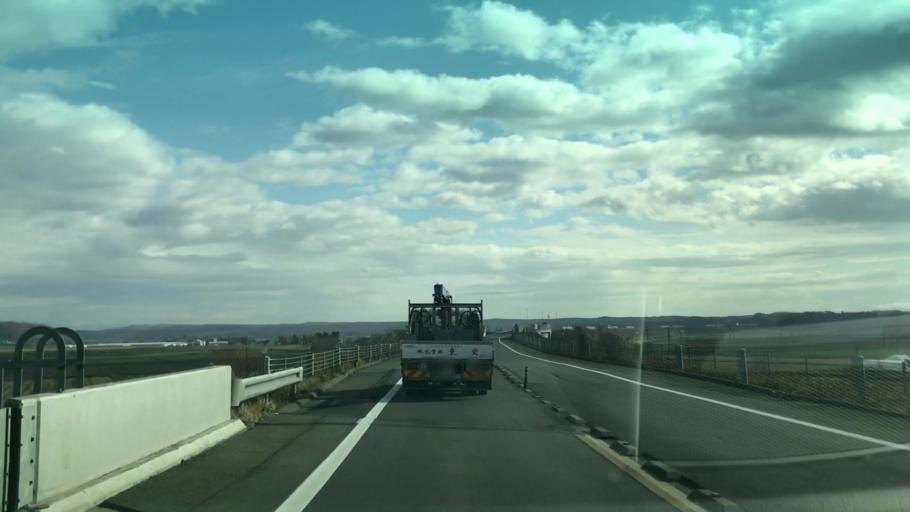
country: JP
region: Hokkaido
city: Tomakomai
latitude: 42.5772
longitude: 141.9637
